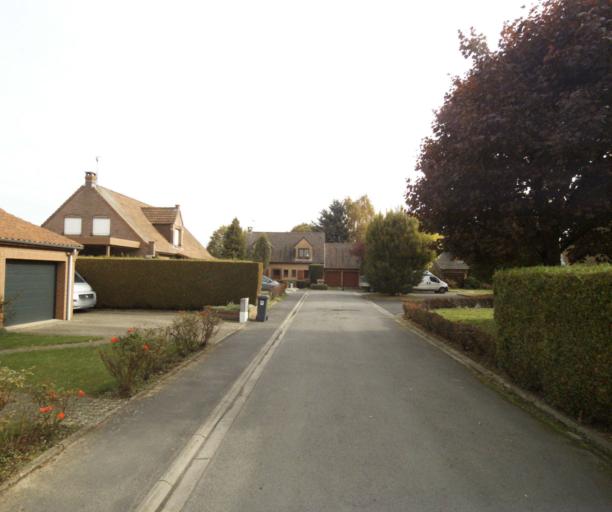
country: FR
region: Nord-Pas-de-Calais
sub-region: Departement du Nord
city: Herlies
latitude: 50.6082
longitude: 2.8559
